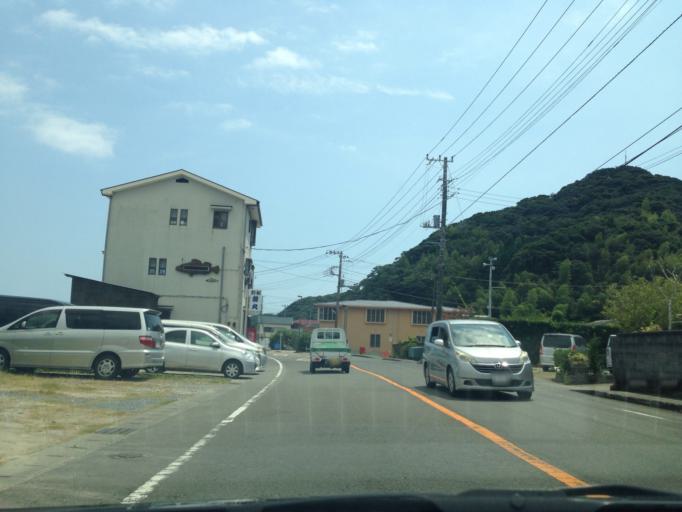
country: JP
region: Shizuoka
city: Shimoda
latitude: 34.6355
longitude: 138.8851
